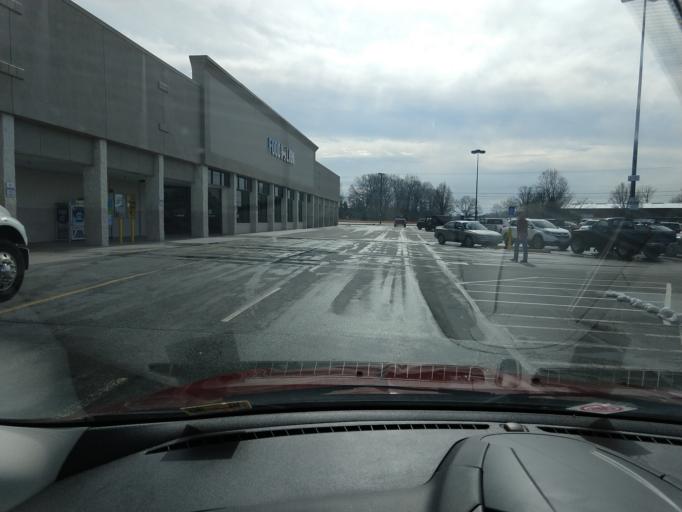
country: US
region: Virginia
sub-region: Amherst County
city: Madison Heights
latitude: 37.4677
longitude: -79.1168
